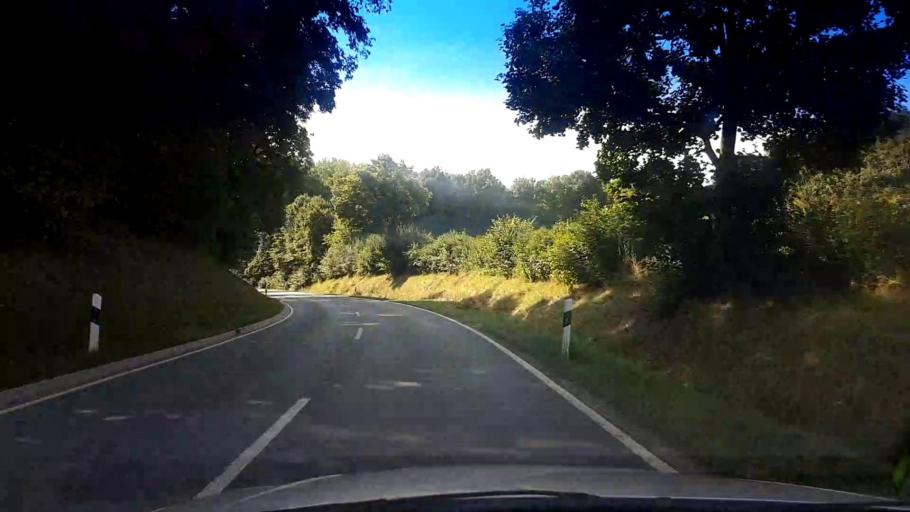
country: DE
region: Bavaria
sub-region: Upper Franconia
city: Hollfeld
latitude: 49.9440
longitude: 11.3350
